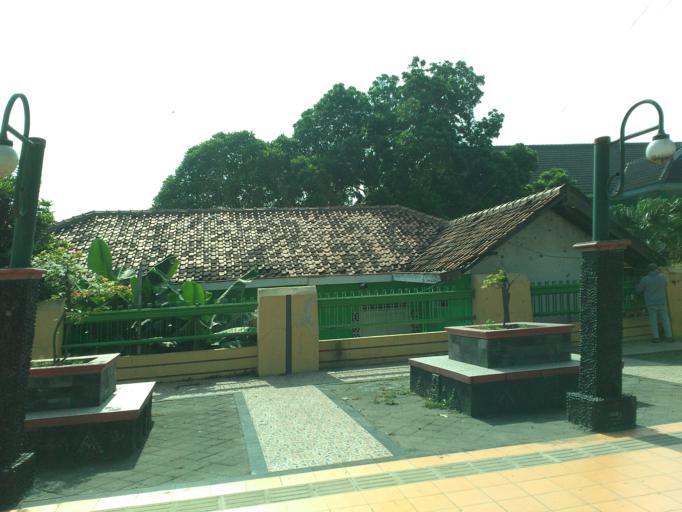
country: ID
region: Central Java
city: Delanggu
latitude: -7.6229
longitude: 110.6979
